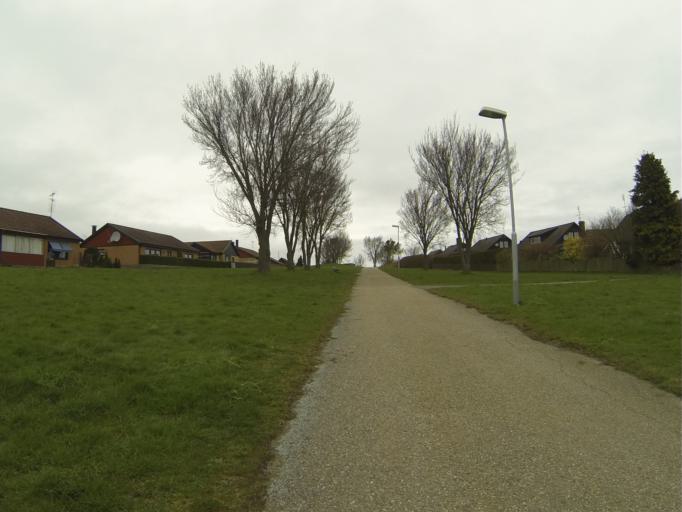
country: SE
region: Skane
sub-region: Simrishamns Kommun
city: Simrishamn
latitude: 55.5406
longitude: 14.3479
